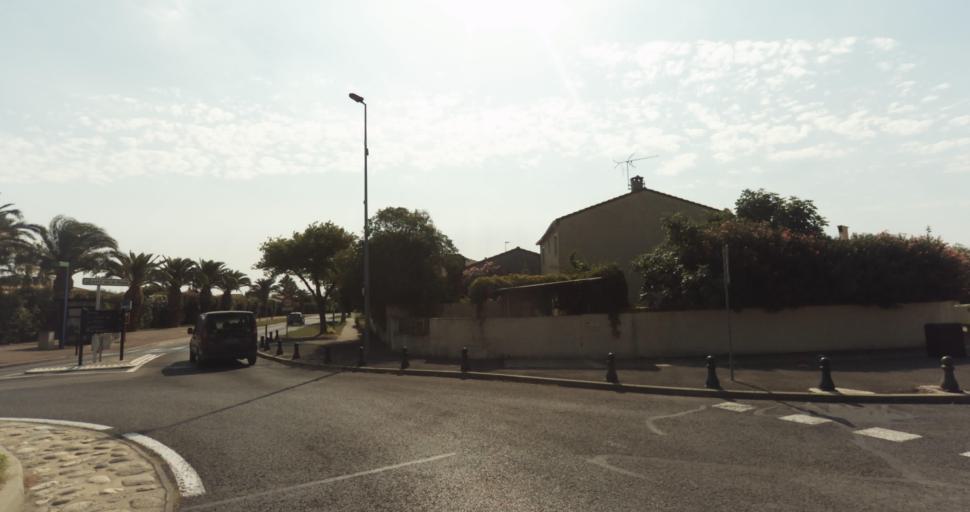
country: FR
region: Languedoc-Roussillon
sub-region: Departement des Pyrenees-Orientales
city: Latour-Bas-Elne
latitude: 42.6186
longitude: 3.0117
